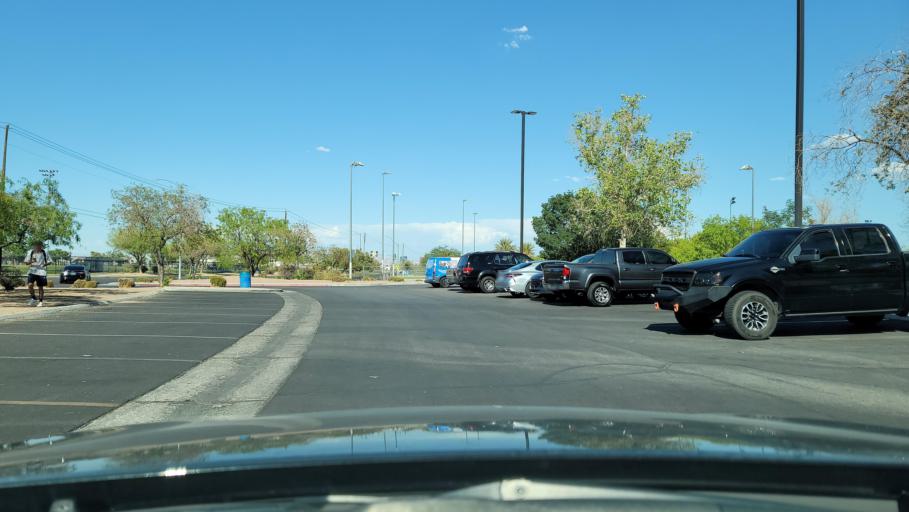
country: US
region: Nevada
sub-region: Clark County
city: Spring Valley
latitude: 36.1254
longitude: -115.2763
